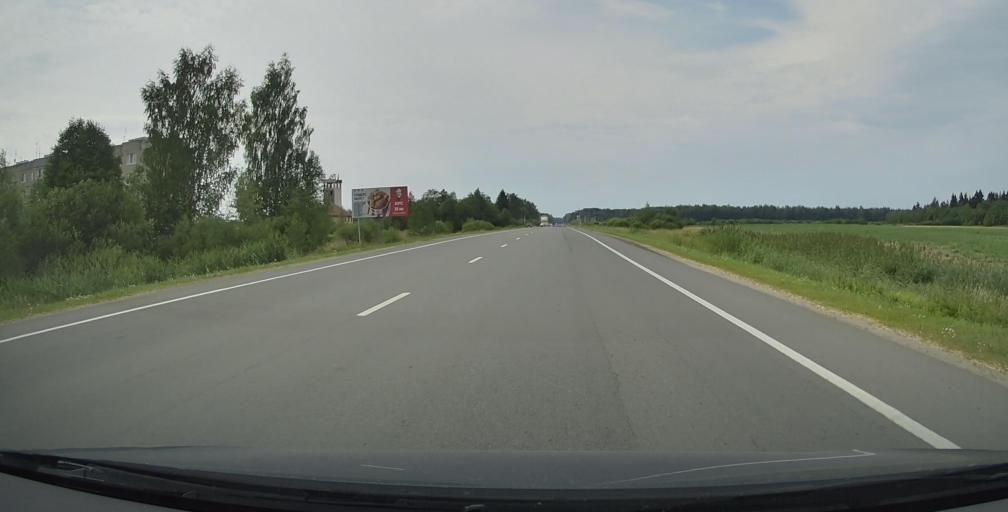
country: RU
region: Jaroslavl
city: Pesochnoye
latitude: 57.9876
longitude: 39.1074
